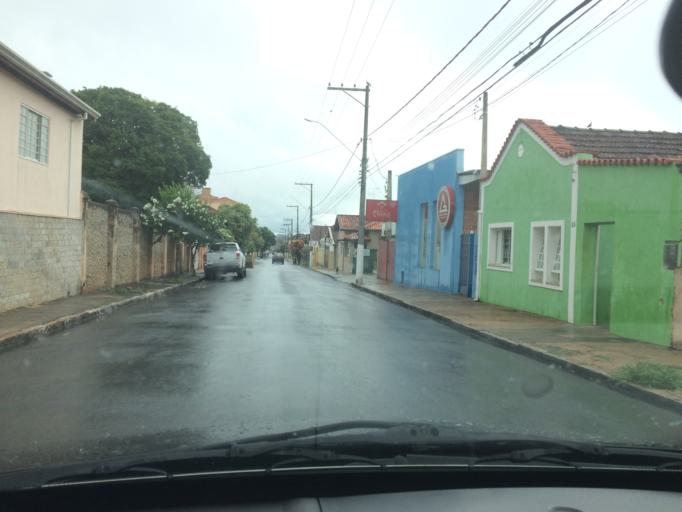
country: BR
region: Sao Paulo
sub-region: Casa Branca
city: Casa Branca
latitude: -21.7734
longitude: -47.0826
